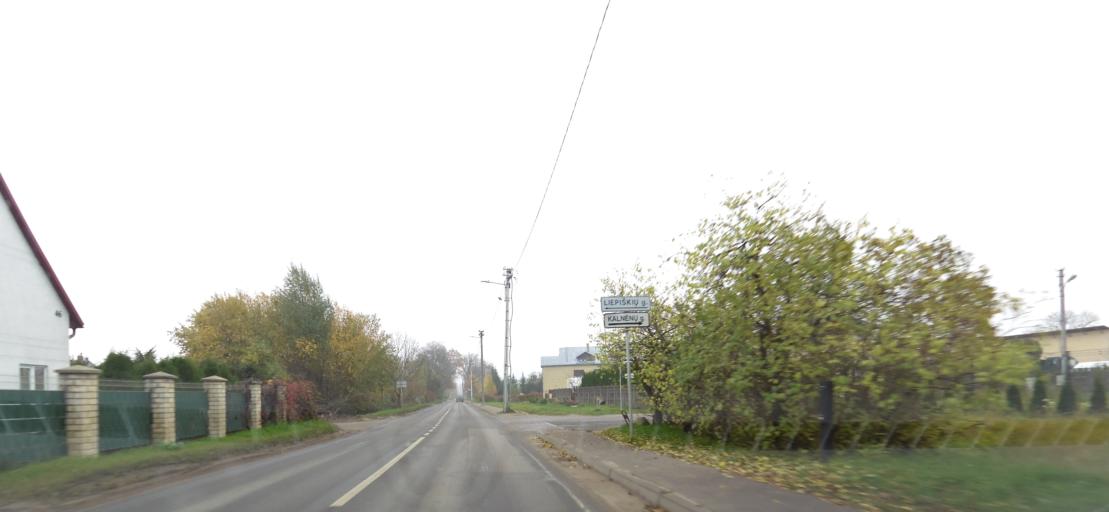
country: LT
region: Vilnius County
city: Rasos
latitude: 54.6619
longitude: 25.3457
